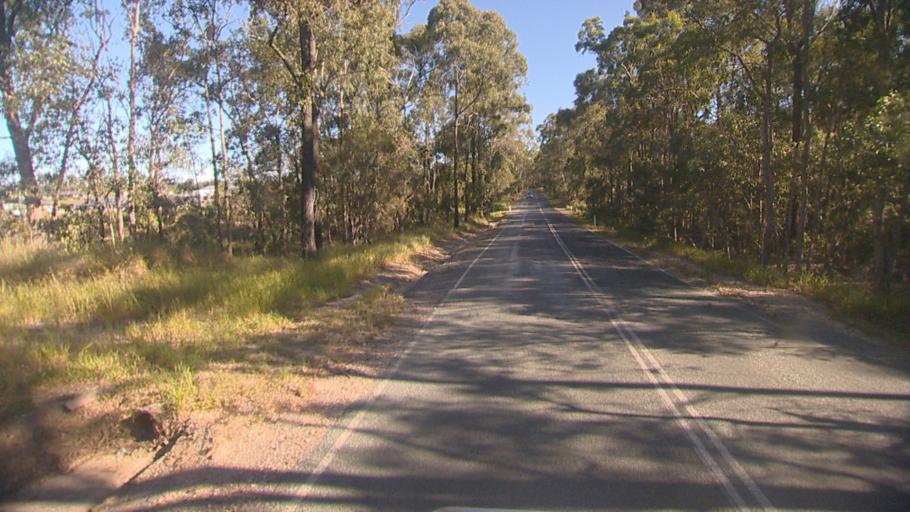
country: AU
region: Queensland
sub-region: Logan
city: Logan Reserve
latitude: -27.7470
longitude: 153.1339
